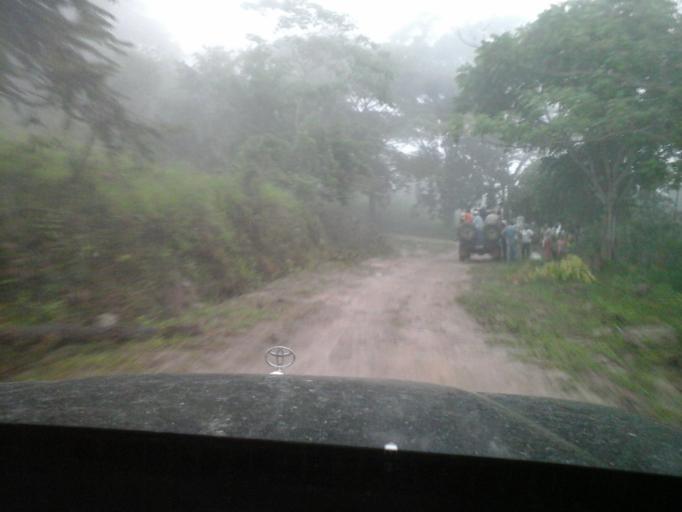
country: CO
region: Cesar
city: Agustin Codazzi
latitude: 9.9384
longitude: -73.1468
